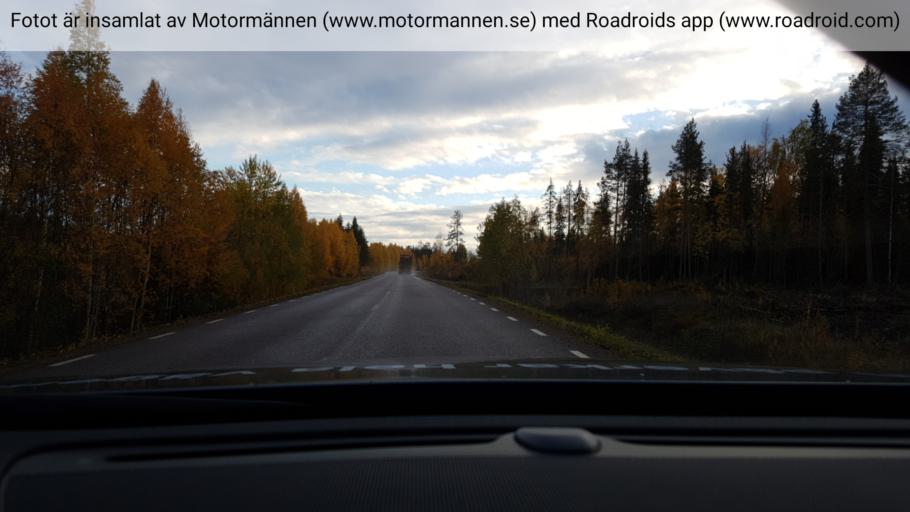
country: SE
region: Norrbotten
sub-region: Overkalix Kommun
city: OEverkalix
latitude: 66.8141
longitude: 22.7423
